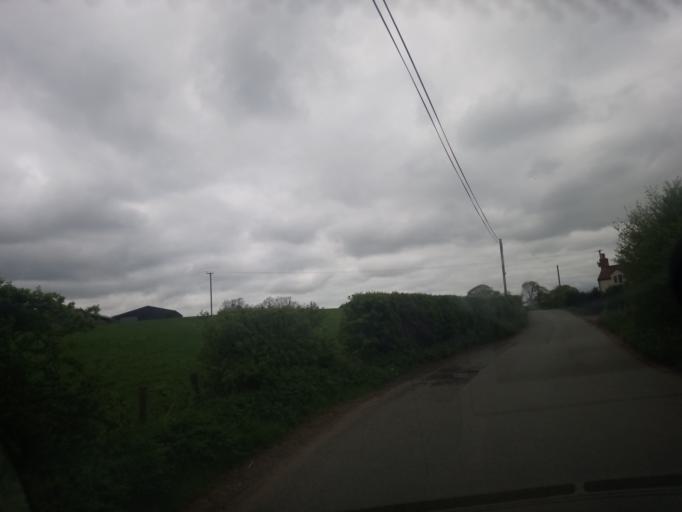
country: GB
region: England
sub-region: Shropshire
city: Stoke upon Tern
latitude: 52.8463
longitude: -2.5472
